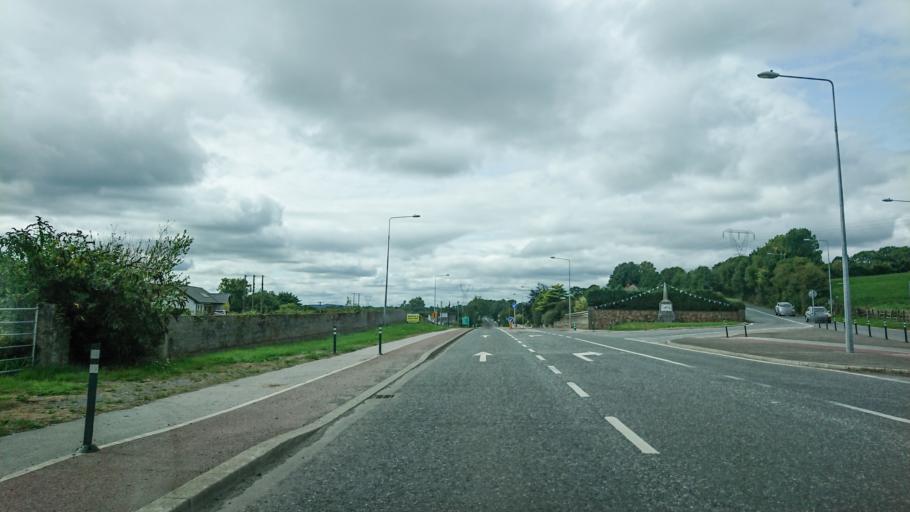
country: IE
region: Munster
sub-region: Waterford
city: Dungarvan
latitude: 52.1092
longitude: -7.6722
